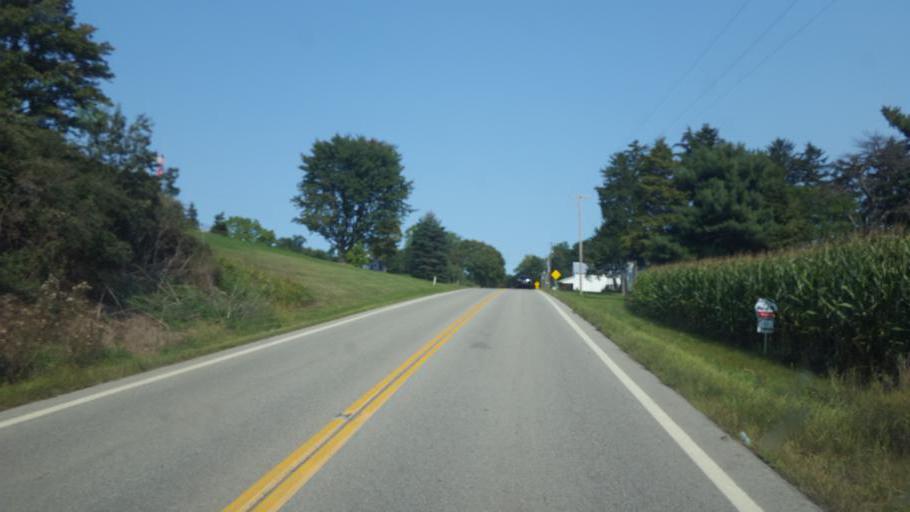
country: US
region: Ohio
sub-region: Wayne County
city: Shreve
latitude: 40.7037
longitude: -82.0958
